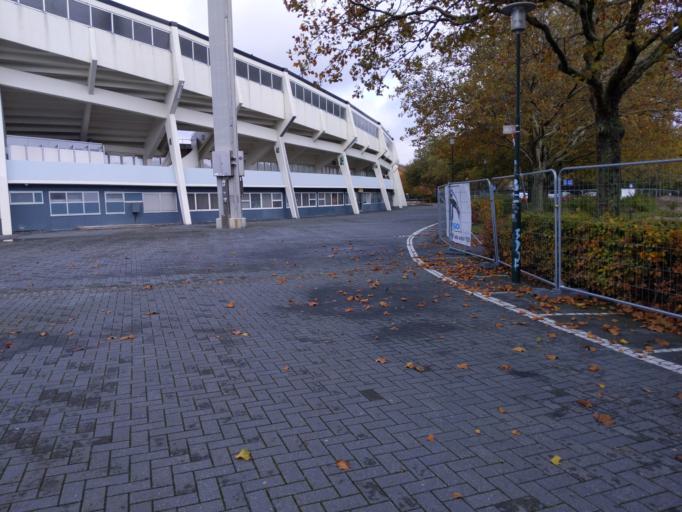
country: SE
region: Skane
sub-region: Malmo
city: Malmoe
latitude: 55.5850
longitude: 12.9897
